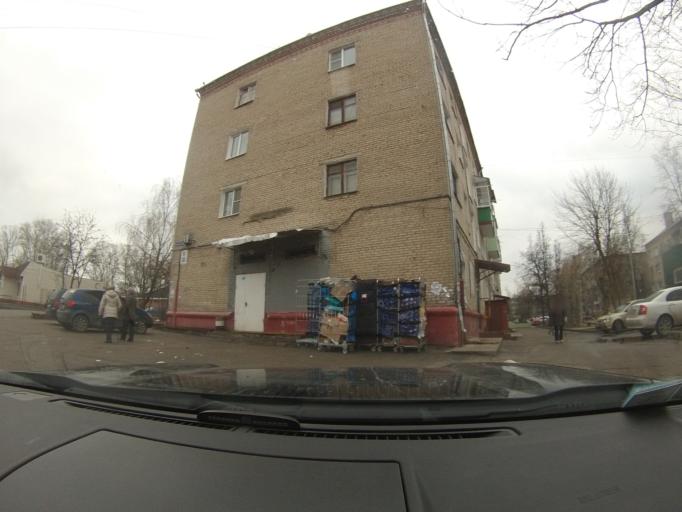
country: RU
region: Moskovskaya
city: Lopatinskiy
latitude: 55.3419
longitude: 38.7253
